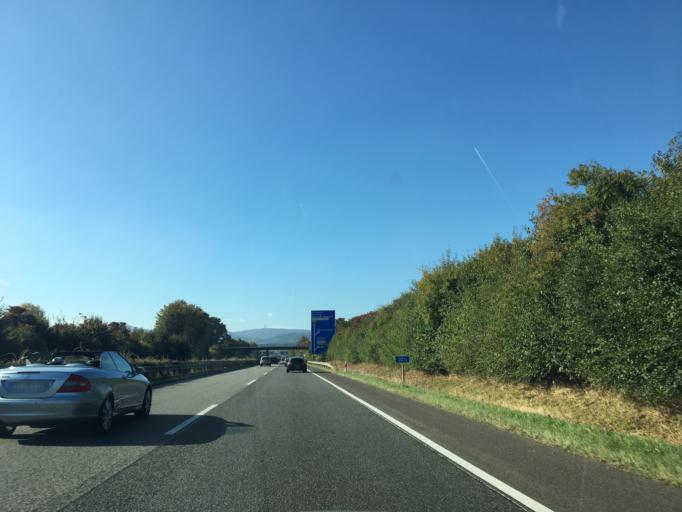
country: DE
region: Hesse
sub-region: Regierungsbezirk Darmstadt
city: Oberursel
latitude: 50.2130
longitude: 8.5910
